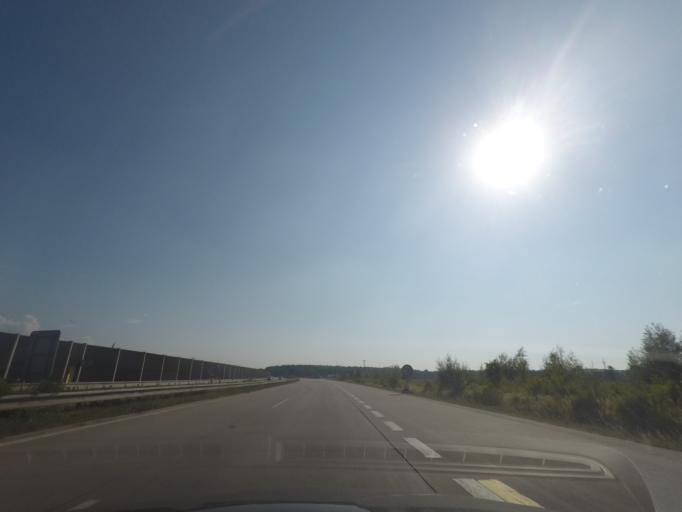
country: PL
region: Silesian Voivodeship
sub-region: Powiat raciborski
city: Chalupki
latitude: 49.9074
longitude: 18.3120
